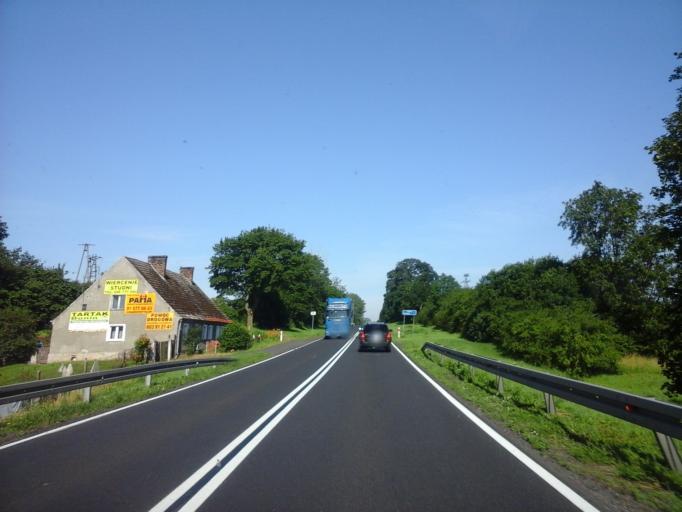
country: PL
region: West Pomeranian Voivodeship
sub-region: Powiat stargardzki
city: Dolice
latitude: 53.2943
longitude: 15.1969
